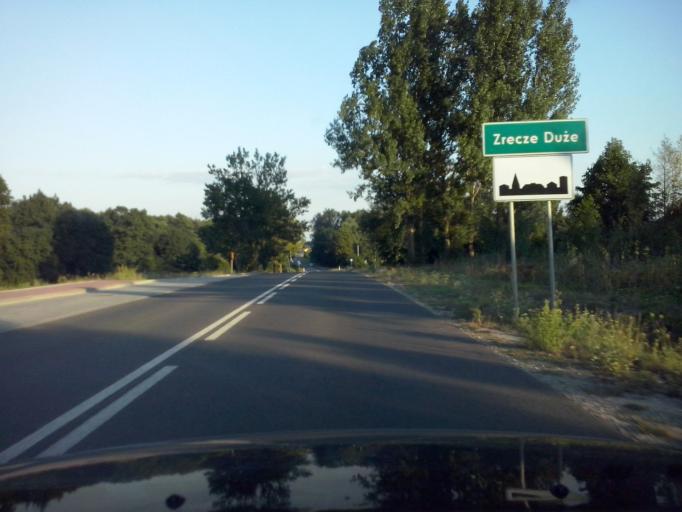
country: PL
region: Swietokrzyskie
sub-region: Powiat kielecki
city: Chmielnik
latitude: 50.6150
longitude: 20.7871
